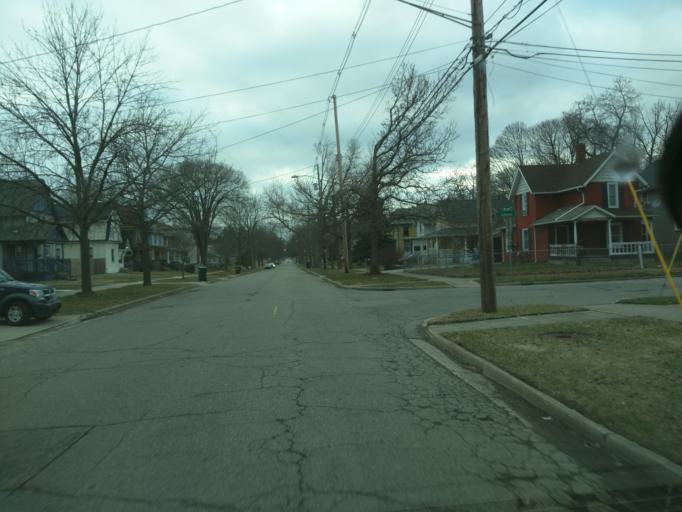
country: US
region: Michigan
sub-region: Ingham County
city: Lansing
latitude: 42.7338
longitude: -84.5702
